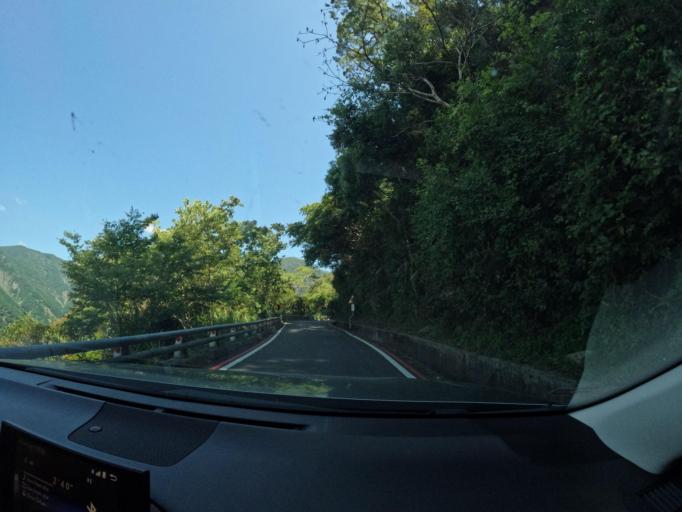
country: TW
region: Taiwan
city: Yujing
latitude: 23.2864
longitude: 120.8487
